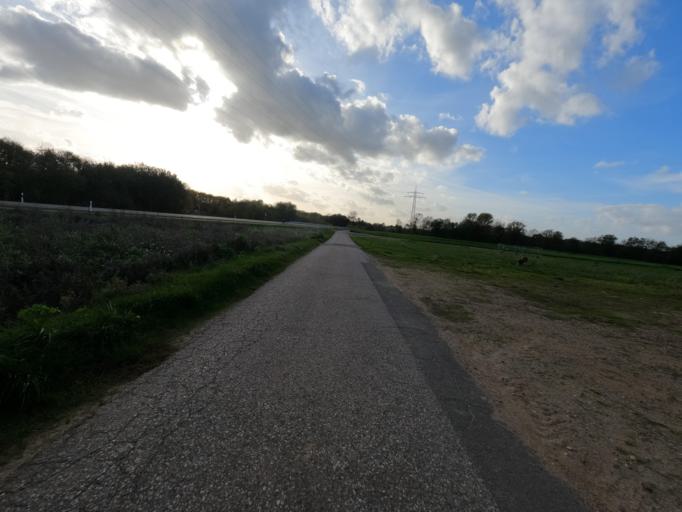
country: DE
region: North Rhine-Westphalia
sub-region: Regierungsbezirk Koln
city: Titz
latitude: 51.0908
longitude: 6.4128
